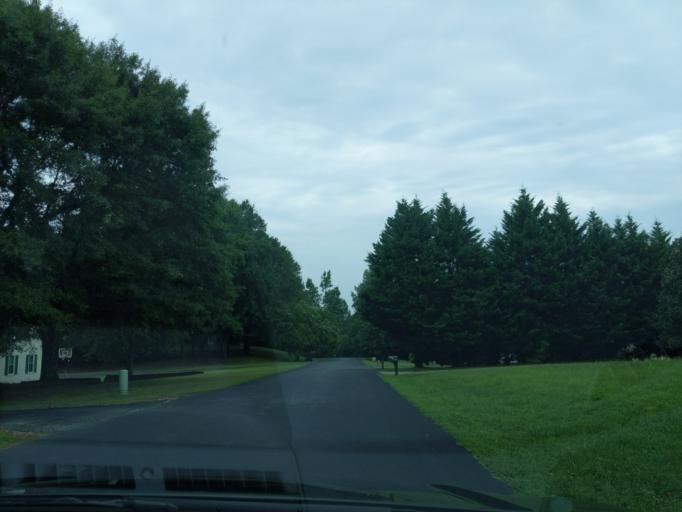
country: US
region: South Carolina
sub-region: Spartanburg County
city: Wellford
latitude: 34.9029
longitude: -82.0798
